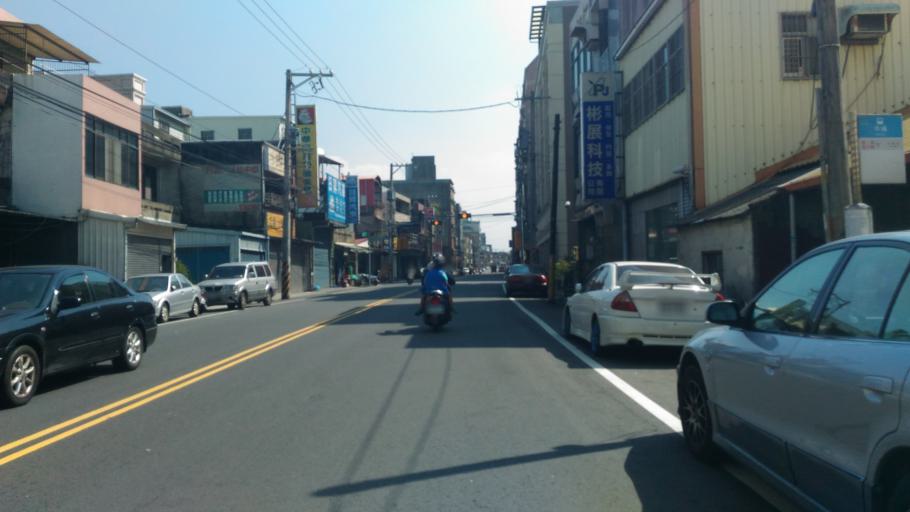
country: TW
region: Taiwan
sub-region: Hsinchu
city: Hsinchu
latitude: 24.8379
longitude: 120.9416
